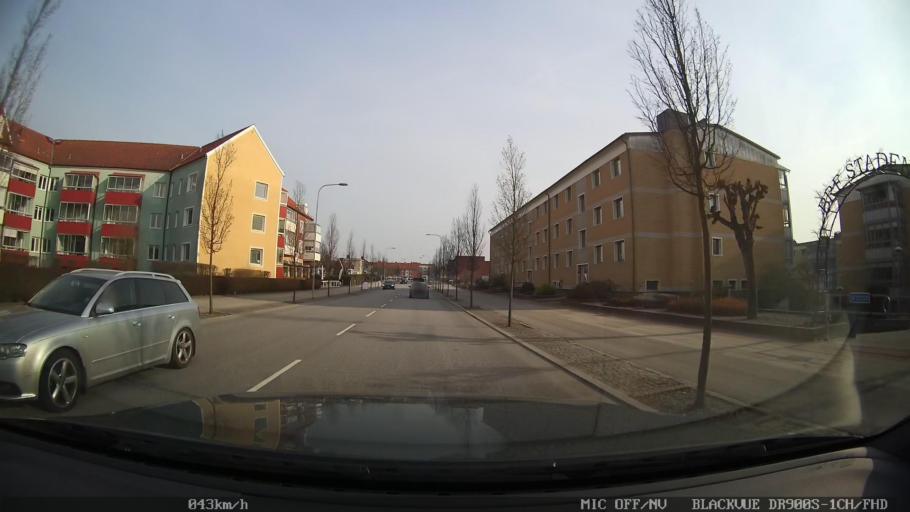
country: SE
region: Skane
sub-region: Ystads Kommun
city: Ystad
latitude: 55.4310
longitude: 13.8038
